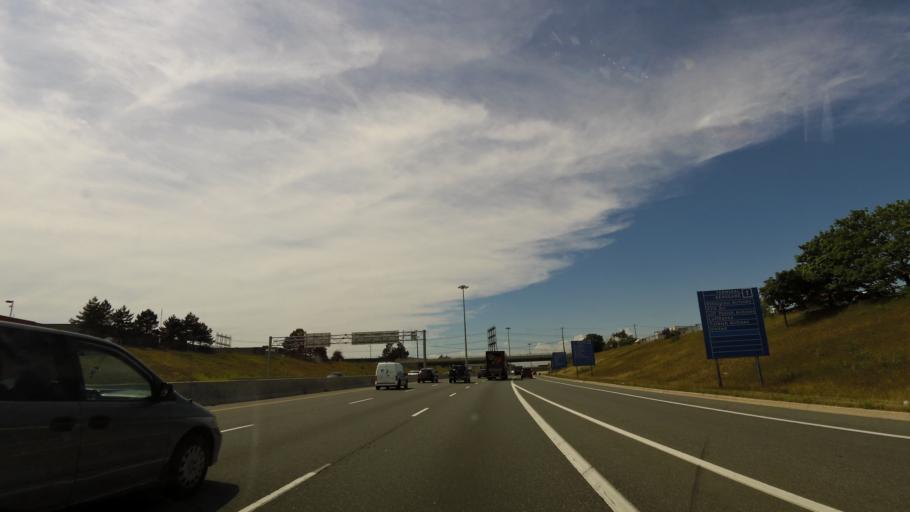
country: CA
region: Ontario
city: Etobicoke
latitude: 43.6987
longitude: -79.5775
